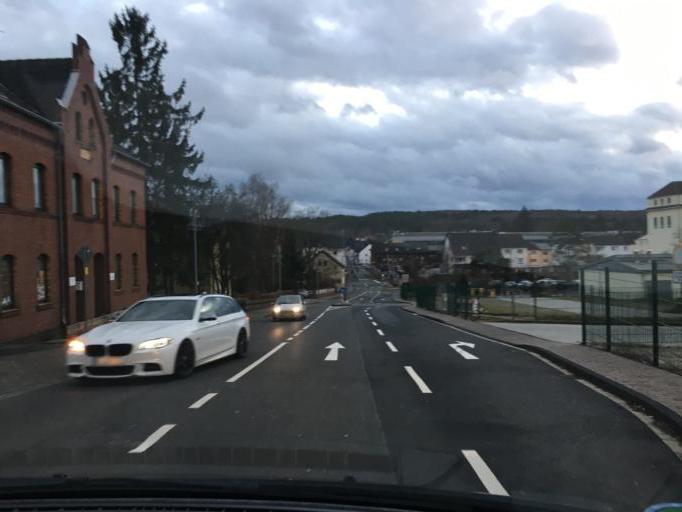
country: DE
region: North Rhine-Westphalia
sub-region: Regierungsbezirk Koln
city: Mechernich
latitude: 50.5933
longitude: 6.6531
